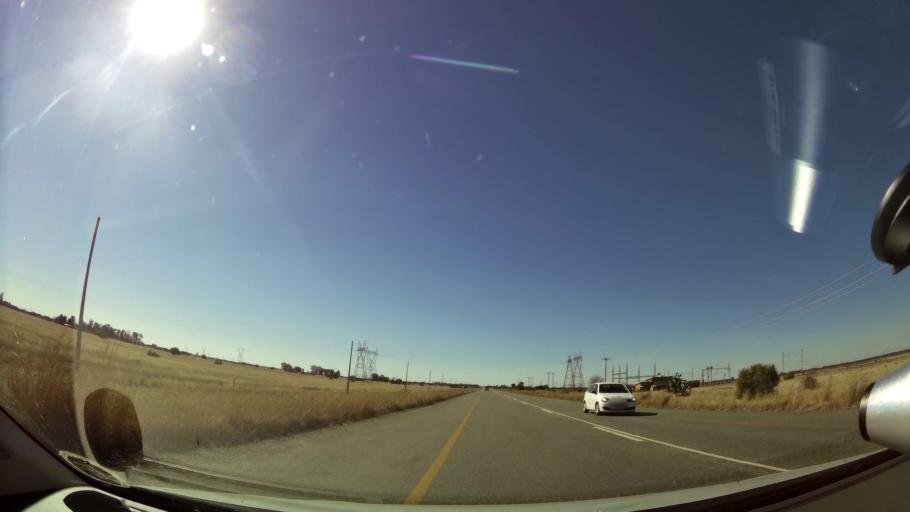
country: ZA
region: North-West
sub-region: Dr Ruth Segomotsi Mompati District Municipality
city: Bloemhof
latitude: -27.6774
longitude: 25.4723
